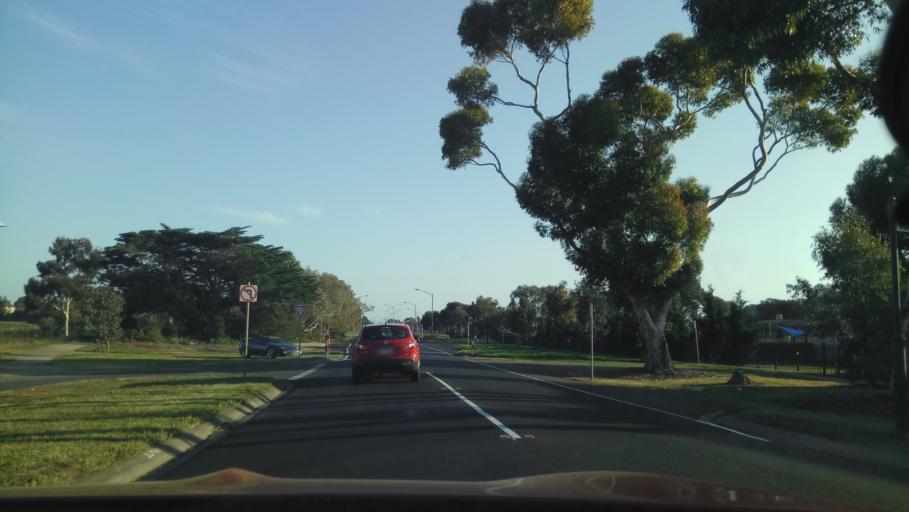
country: AU
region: Victoria
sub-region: Wyndham
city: Point Cook
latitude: -37.8917
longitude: 144.7552
